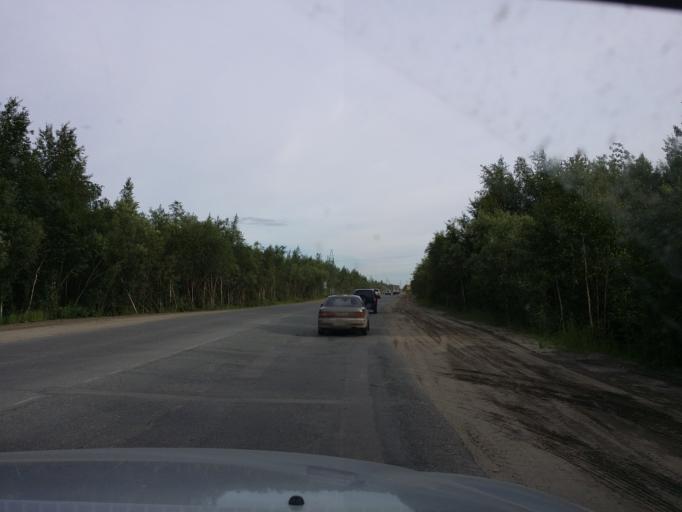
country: RU
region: Khanty-Mansiyskiy Avtonomnyy Okrug
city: Nizhnevartovsk
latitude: 60.9624
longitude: 76.6620
